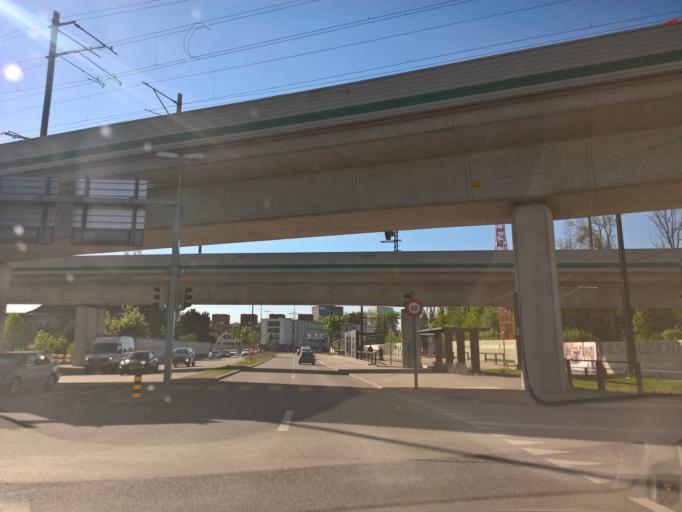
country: CH
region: Zurich
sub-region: Bezirk Buelach
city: Wallisellen / Wallisellen-Ost
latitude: 47.4049
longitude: 8.6037
